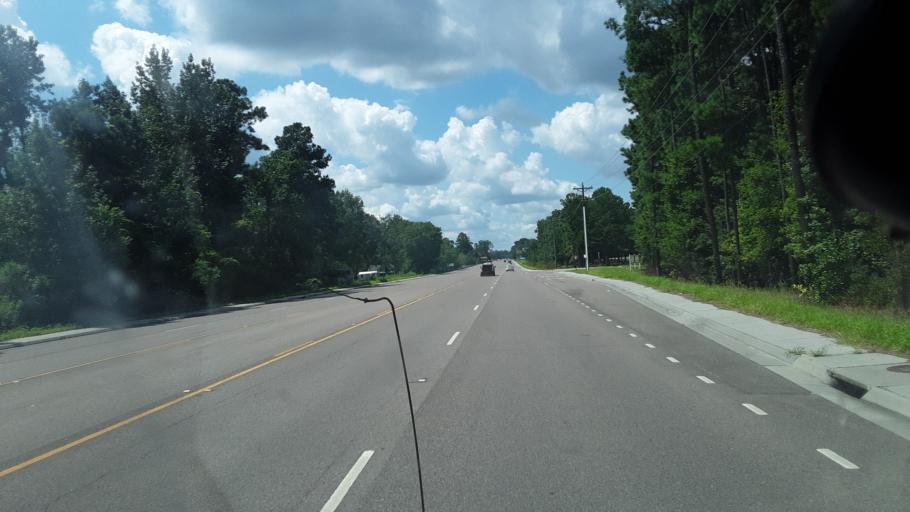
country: US
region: South Carolina
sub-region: Berkeley County
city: Moncks Corner
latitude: 33.1720
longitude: -80.0400
